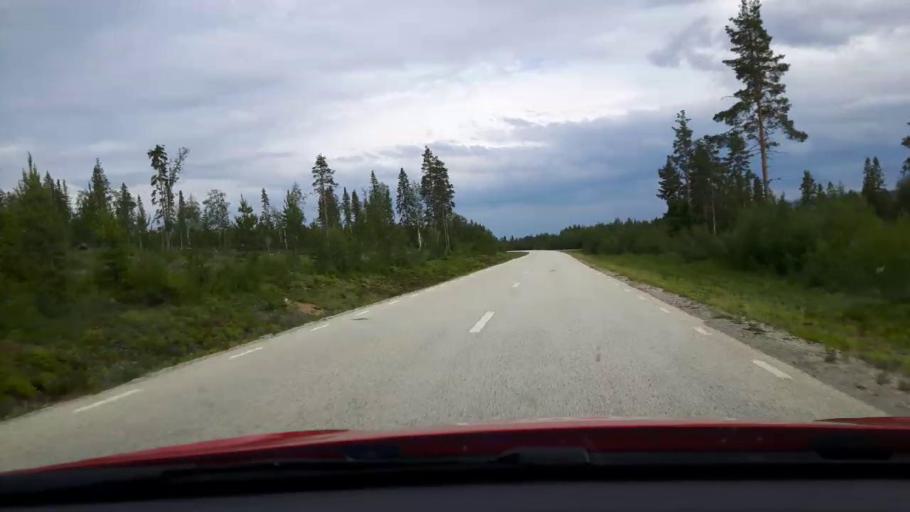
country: SE
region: Jaemtland
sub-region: Bergs Kommun
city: Hoverberg
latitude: 62.7007
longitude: 13.9566
